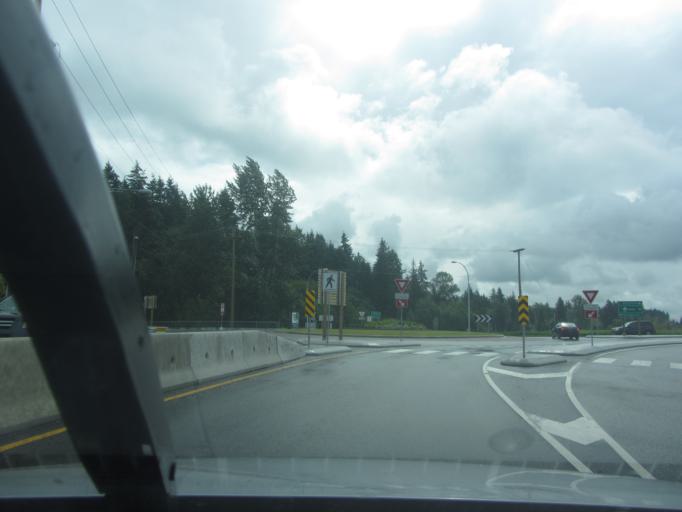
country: CA
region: British Columbia
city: Langley
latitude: 49.1383
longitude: -122.5820
